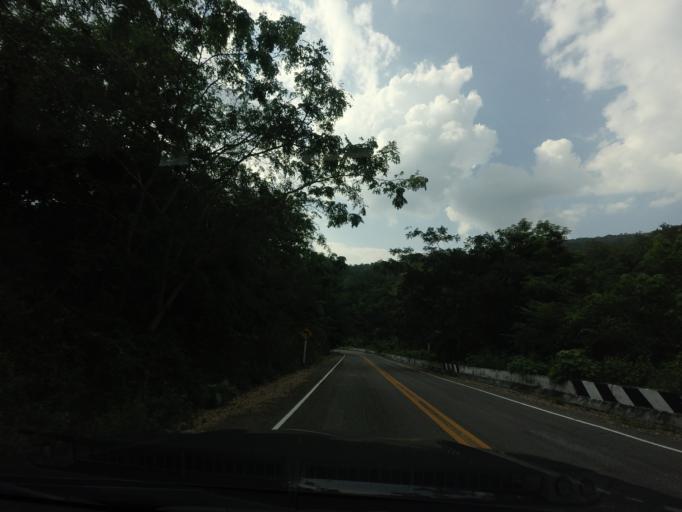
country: TH
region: Nan
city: Na Noi
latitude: 18.2910
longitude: 100.9173
